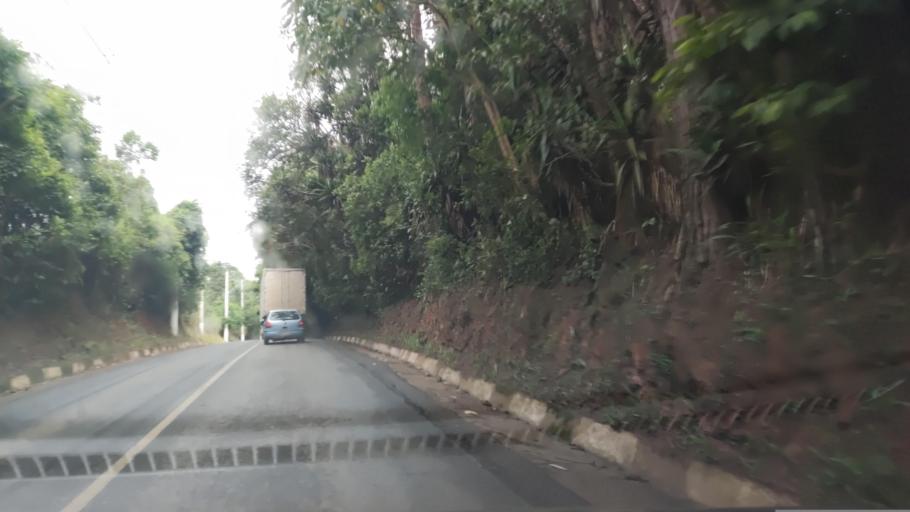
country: BR
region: Sao Paulo
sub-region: Vargem Grande Paulista
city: Vargem Grande Paulista
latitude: -23.6509
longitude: -47.0505
